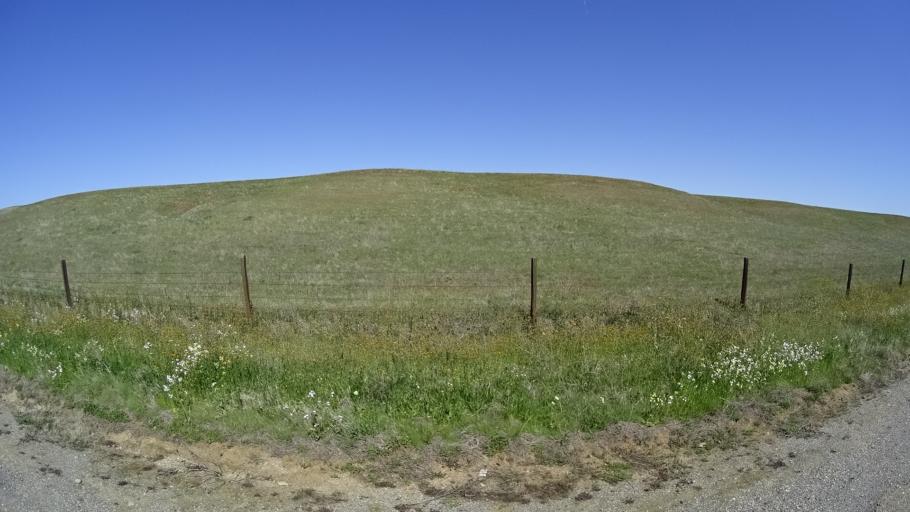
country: US
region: California
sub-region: Glenn County
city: Orland
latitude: 39.7802
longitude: -122.3013
